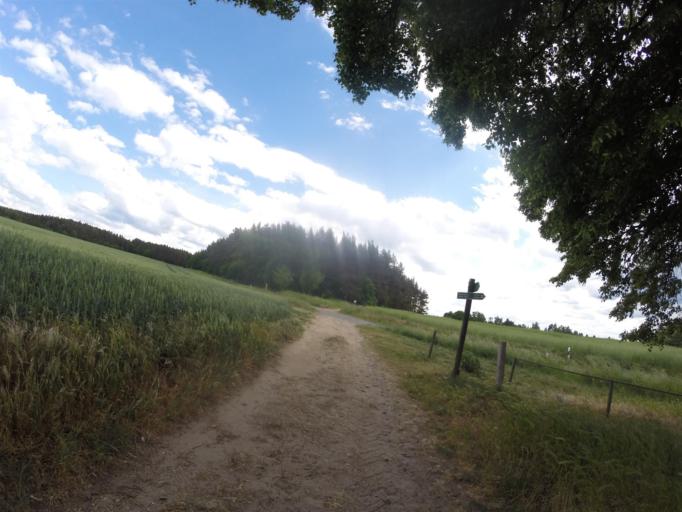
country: DE
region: Thuringia
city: Zollnitz
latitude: 50.8599
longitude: 11.6323
